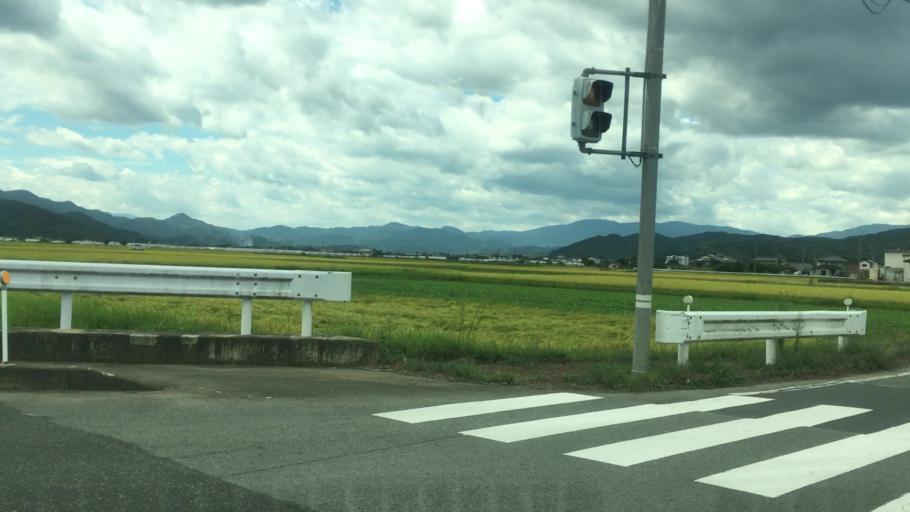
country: JP
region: Hyogo
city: Toyooka
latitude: 35.5247
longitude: 134.8398
